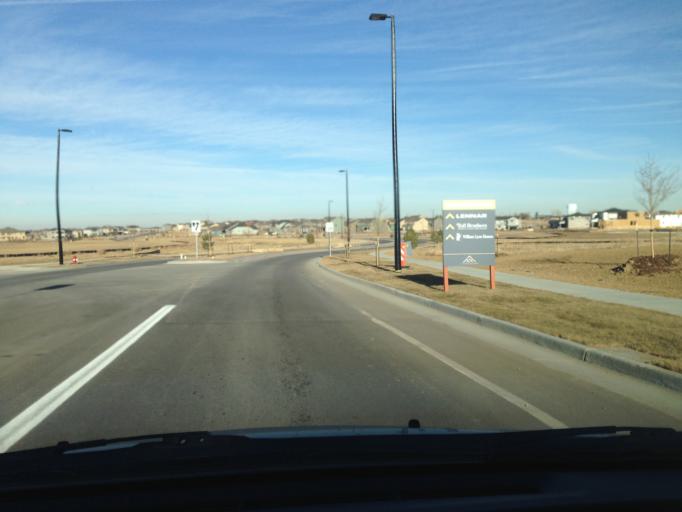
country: US
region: Colorado
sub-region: Boulder County
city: Lafayette
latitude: 40.0224
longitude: -105.0906
